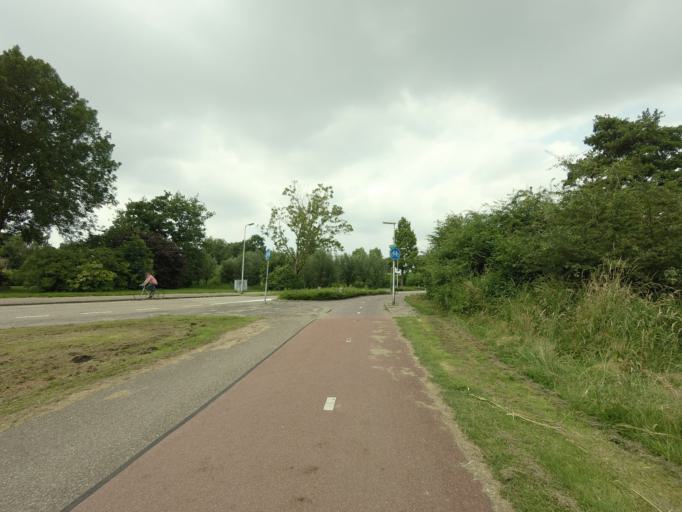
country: NL
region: South Holland
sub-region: Gemeente Krimpen aan den IJssel
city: Krimpen aan den IJssel
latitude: 51.9160
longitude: 4.6116
